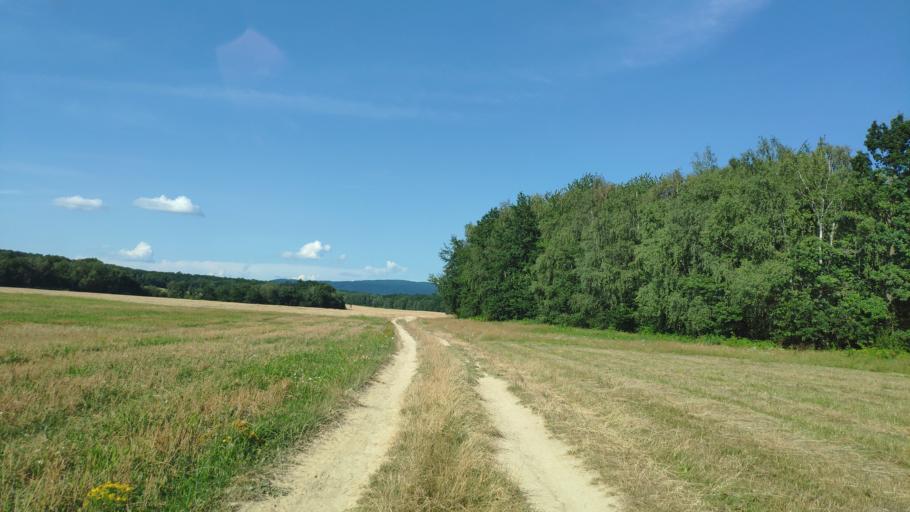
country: SK
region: Presovsky
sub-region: Okres Presov
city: Presov
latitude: 48.9121
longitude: 21.2956
